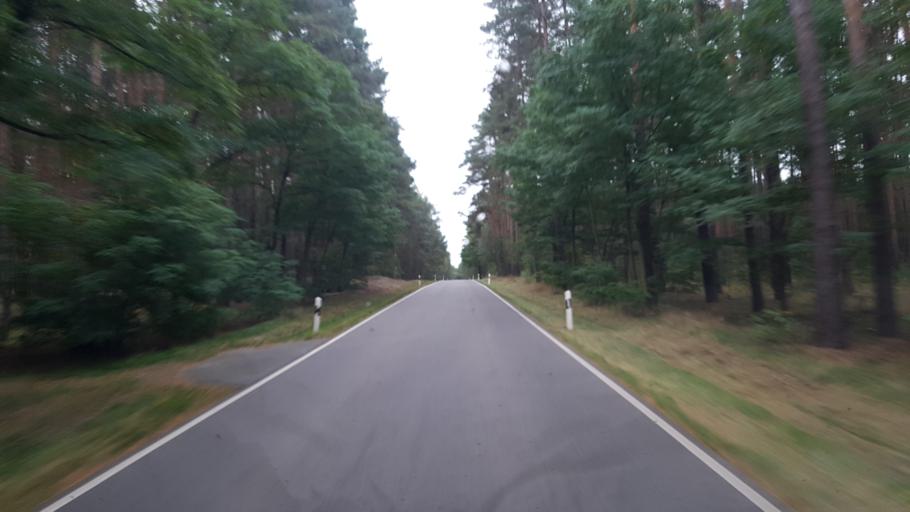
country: DE
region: Brandenburg
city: Luckau
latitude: 51.8851
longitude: 13.6678
